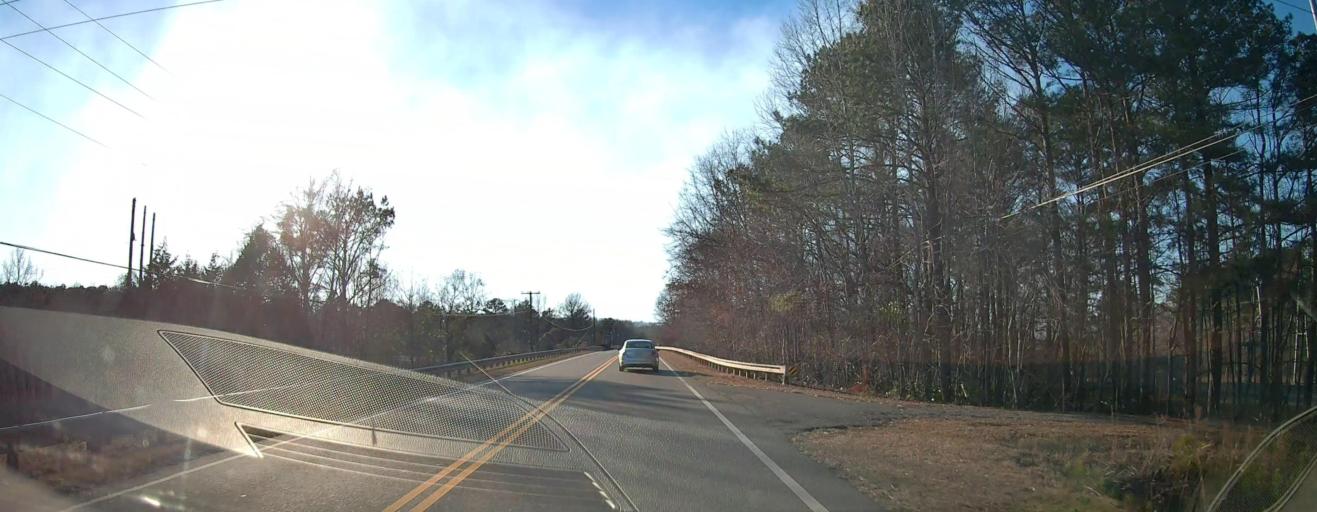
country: US
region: Georgia
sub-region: Meriwether County
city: Manchester
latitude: 32.8776
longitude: -84.6512
